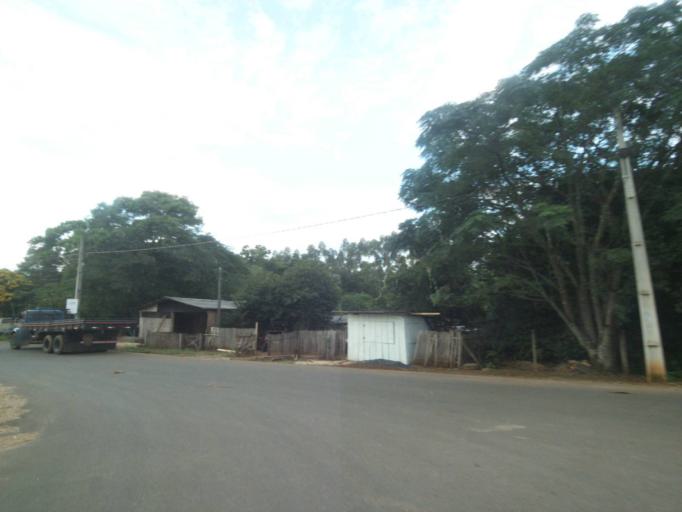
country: BR
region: Parana
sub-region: Telemaco Borba
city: Telemaco Borba
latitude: -24.3840
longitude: -50.6633
